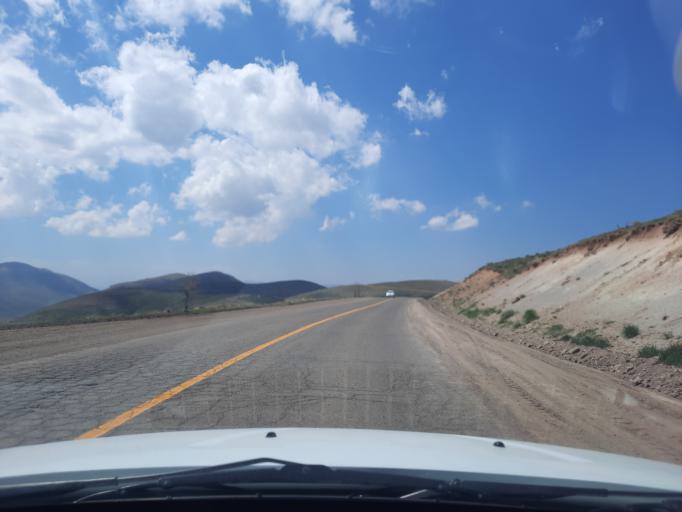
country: IR
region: Qazvin
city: Qazvin
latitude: 36.3889
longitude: 50.2104
